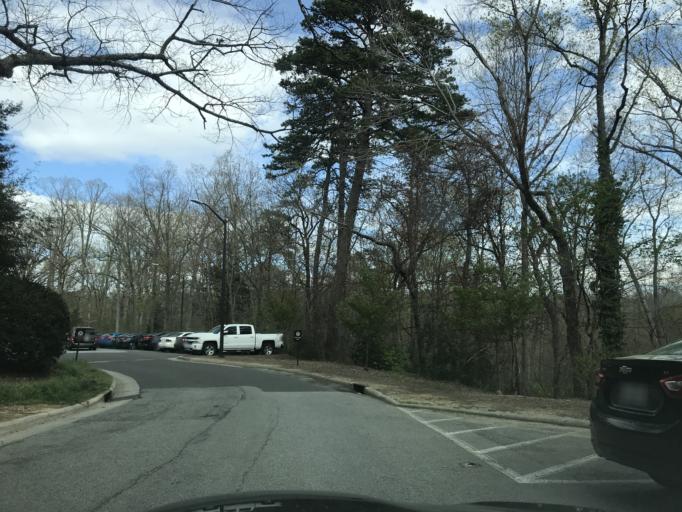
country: US
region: North Carolina
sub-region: Orange County
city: Chapel Hill
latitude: 35.9039
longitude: -79.0427
